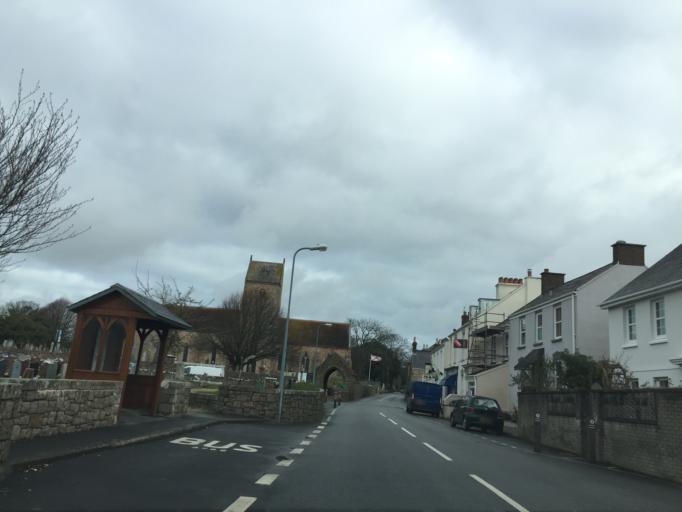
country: JE
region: St Helier
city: Saint Helier
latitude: 49.2136
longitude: -2.1413
